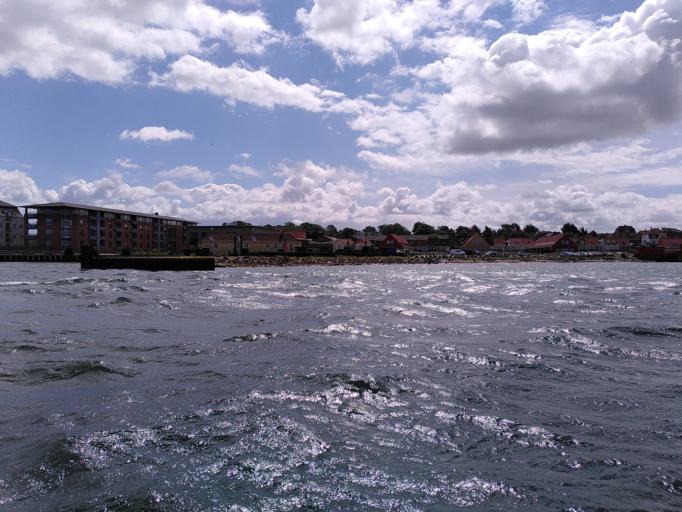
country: DK
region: South Denmark
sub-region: Langeland Kommune
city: Rudkobing
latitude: 54.9381
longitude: 10.7012
